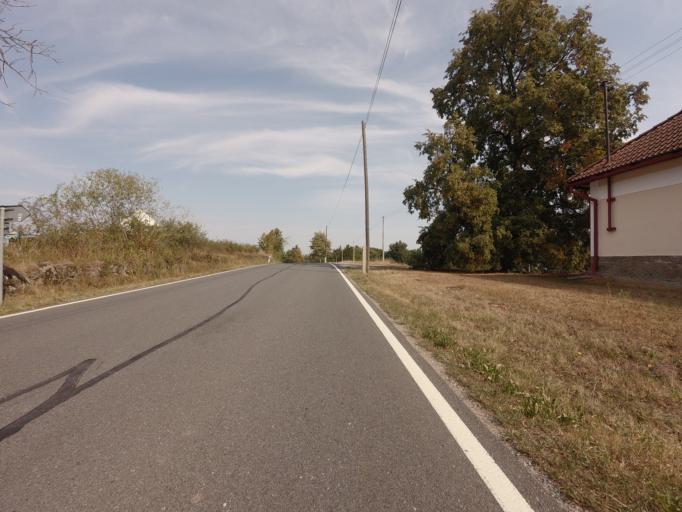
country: CZ
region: Central Bohemia
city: Petrovice
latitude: 49.5444
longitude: 14.3474
